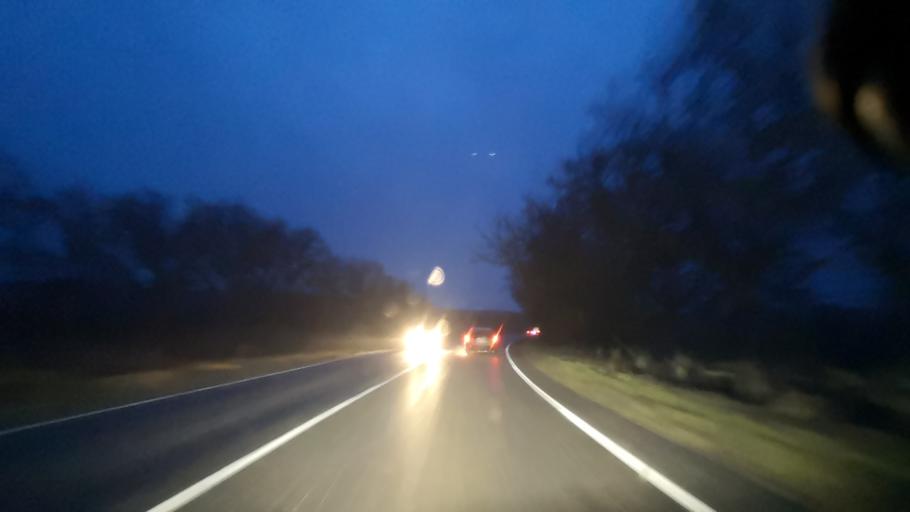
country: MD
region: Orhei
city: Orhei
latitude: 47.4955
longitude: 28.7913
